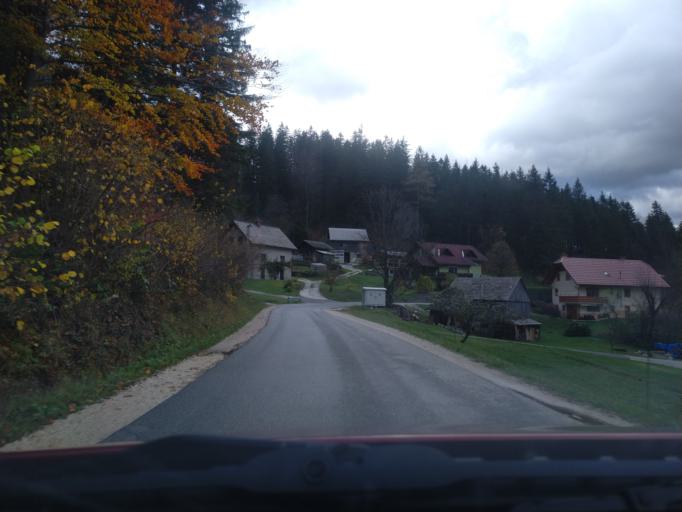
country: SI
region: Luce
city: Luce
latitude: 46.3214
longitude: 14.7075
